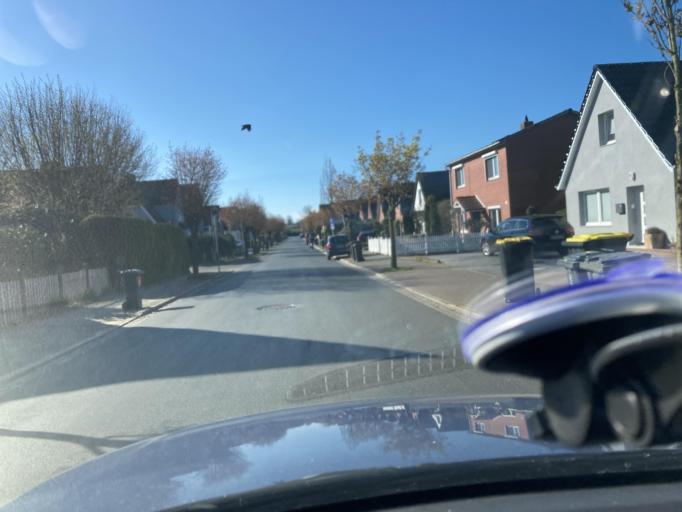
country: DE
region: Schleswig-Holstein
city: Wesseln
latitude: 54.1979
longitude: 9.0825
